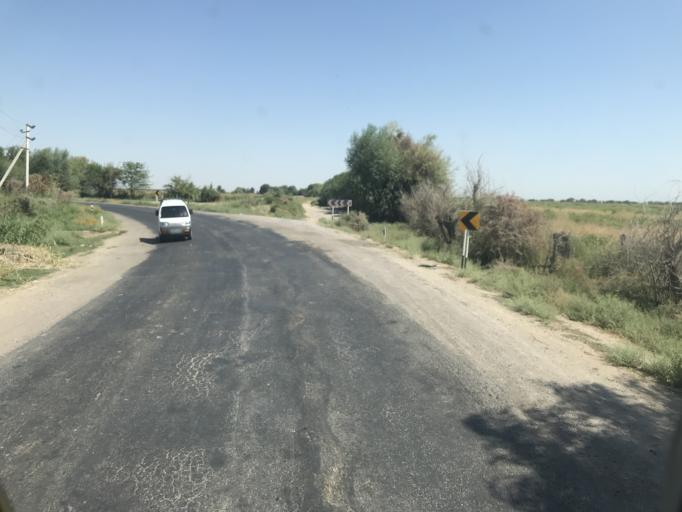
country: KZ
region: Ongtustik Qazaqstan
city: Ilyich
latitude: 40.9474
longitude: 68.4891
